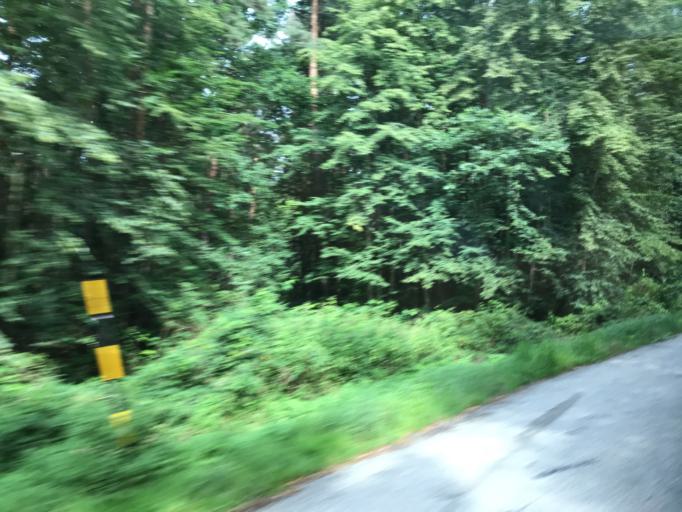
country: CZ
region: Jihocesky
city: Vcelna
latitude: 48.9130
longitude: 14.4511
